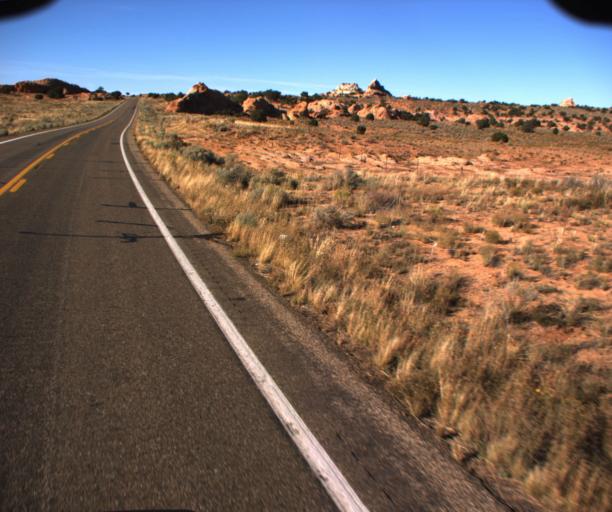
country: US
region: Arizona
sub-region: Coconino County
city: Kaibito
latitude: 36.6228
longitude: -111.2011
